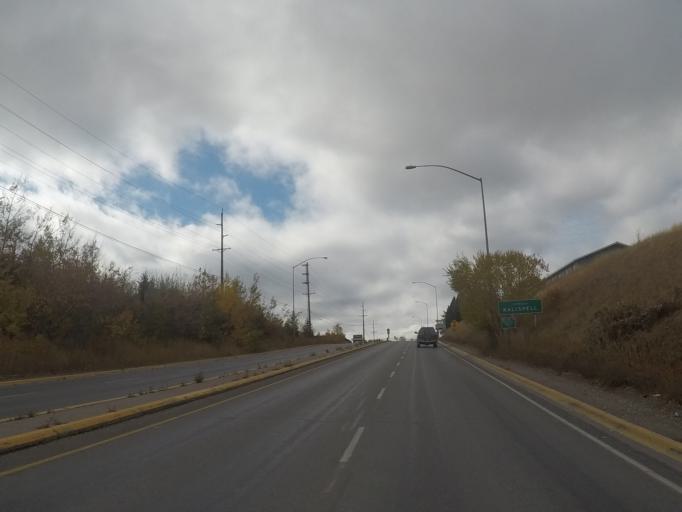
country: US
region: Montana
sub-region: Flathead County
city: Kalispell
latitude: 48.2048
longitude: -114.2988
